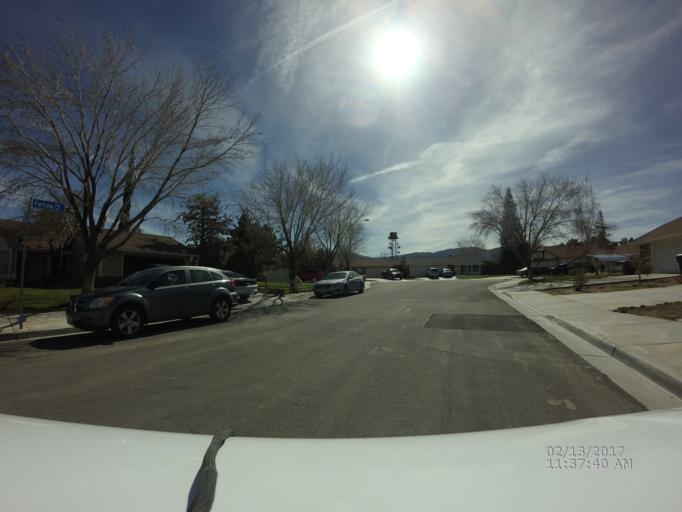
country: US
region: California
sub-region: Los Angeles County
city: Littlerock
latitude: 34.5240
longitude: -117.9984
